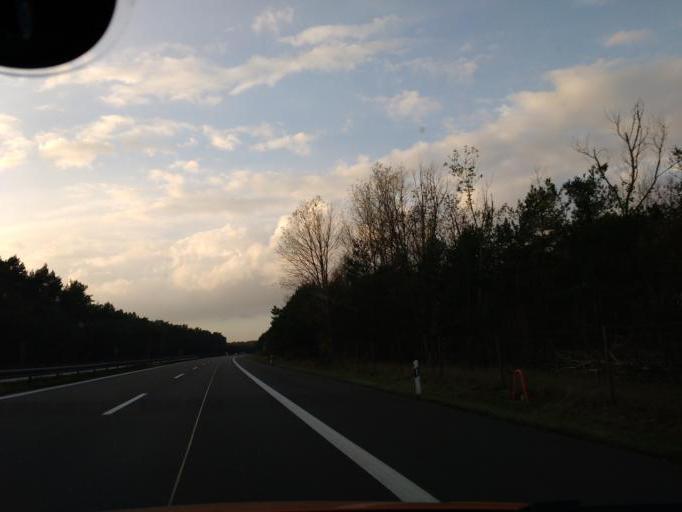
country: DE
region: Mecklenburg-Vorpommern
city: Neustadt-Glewe
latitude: 53.3717
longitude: 11.6463
